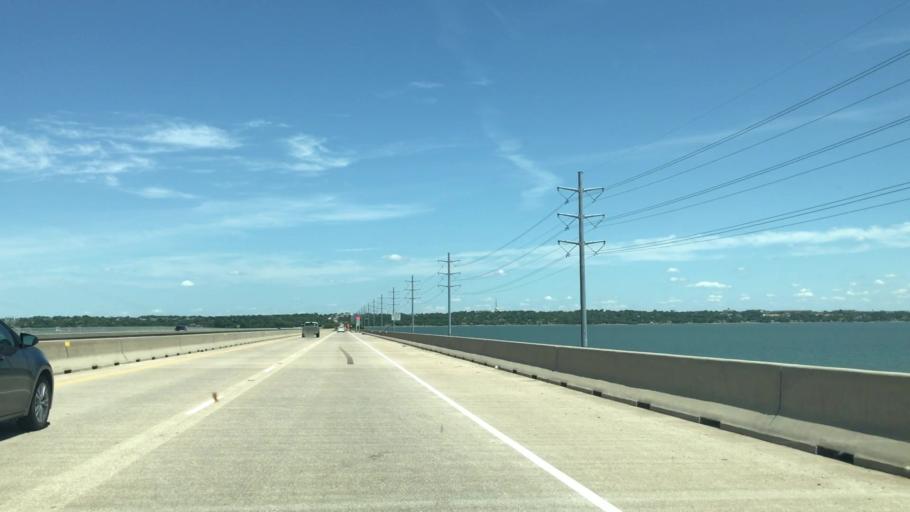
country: US
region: Texas
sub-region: Rockwall County
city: Rockwall
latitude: 32.9218
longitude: -96.5041
